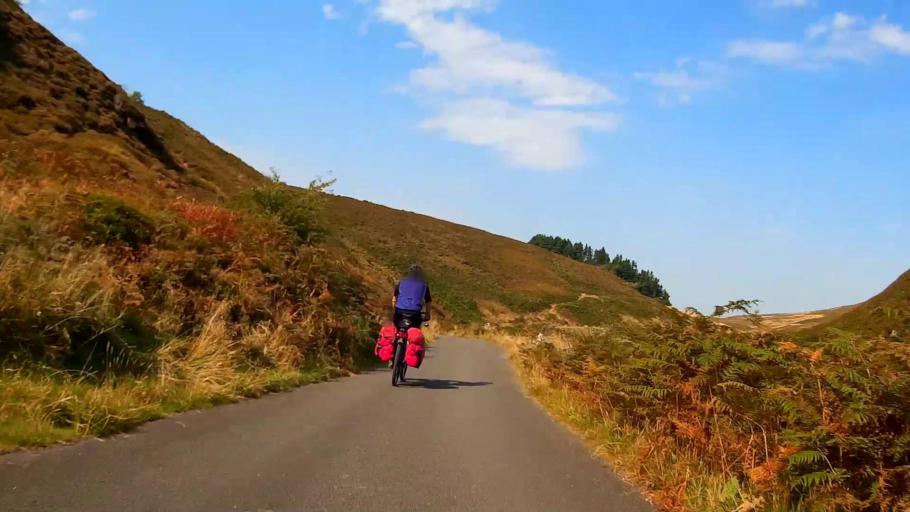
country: GB
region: England
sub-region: Derbyshire
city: Buxton
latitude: 53.2483
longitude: -1.9775
